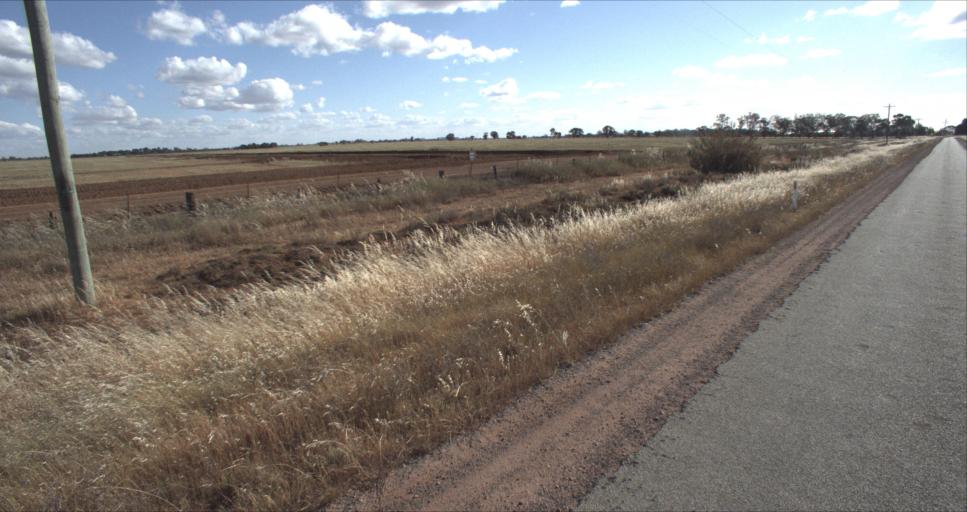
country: AU
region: New South Wales
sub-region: Leeton
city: Leeton
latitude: -34.4592
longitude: 146.2557
